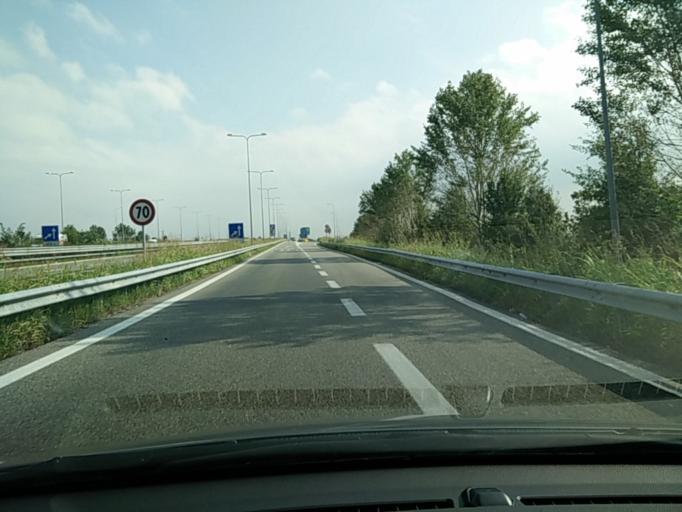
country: IT
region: Lombardy
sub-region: Citta metropolitana di Milano
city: Mesero
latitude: 45.4909
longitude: 8.8441
